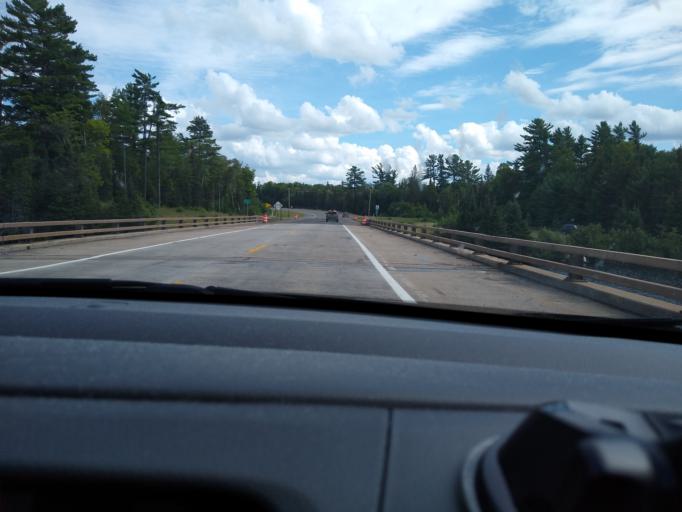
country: US
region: Michigan
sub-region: Marquette County
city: West Ishpeming
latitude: 46.5291
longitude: -88.0033
